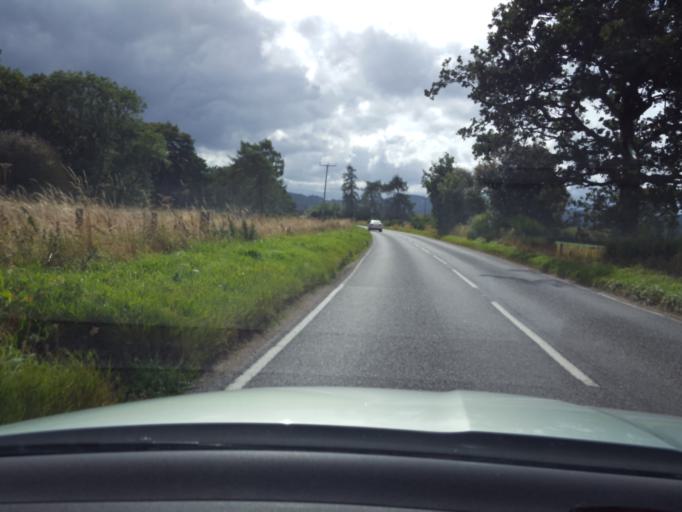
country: GB
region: Scotland
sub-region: Aberdeenshire
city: Ballater
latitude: 57.0559
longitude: -3.0268
